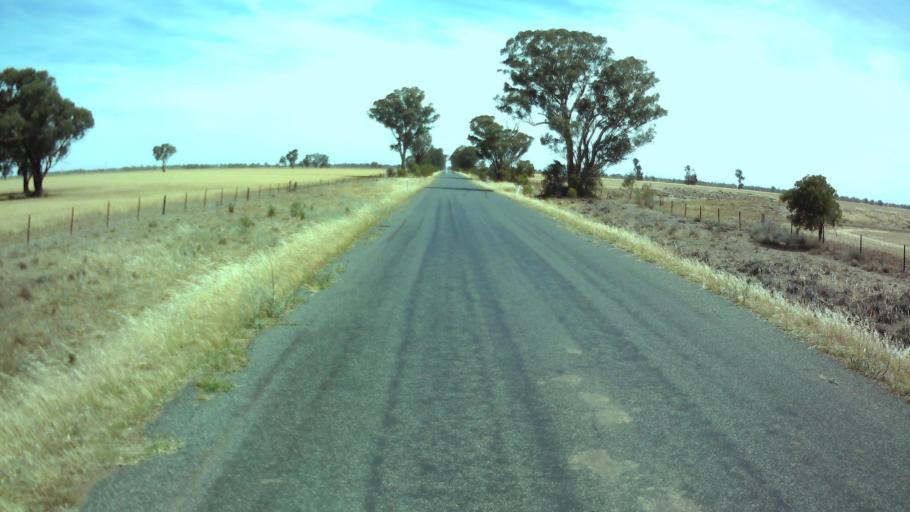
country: AU
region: New South Wales
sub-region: Weddin
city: Grenfell
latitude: -33.9681
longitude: 147.7804
